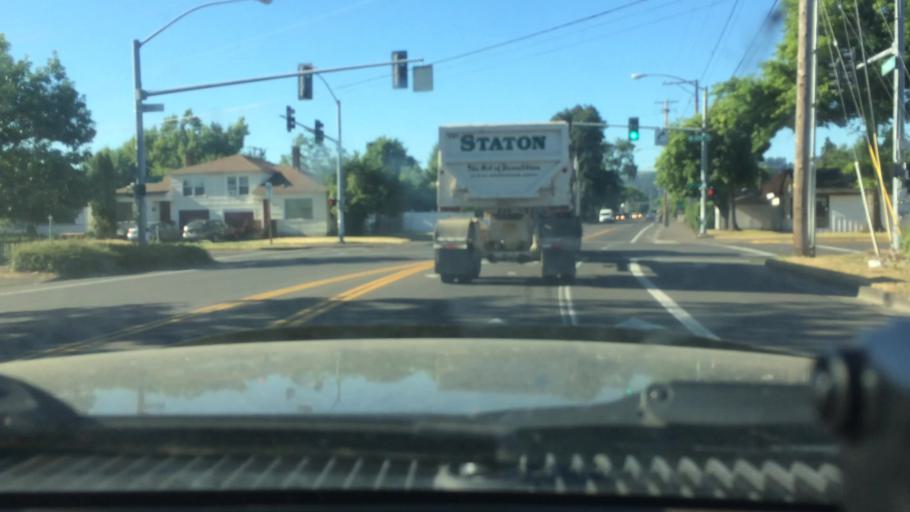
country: US
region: Oregon
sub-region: Lane County
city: Eugene
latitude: 44.0513
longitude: -123.1182
